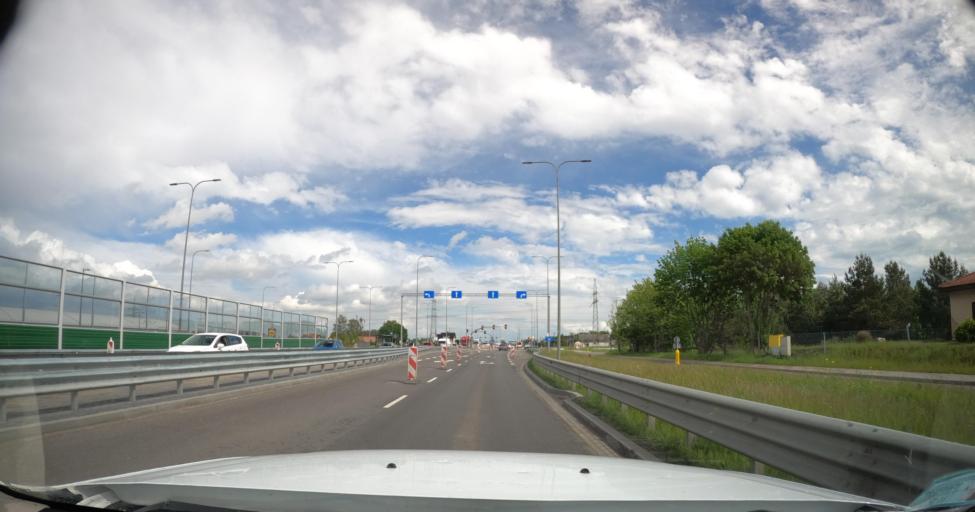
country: PL
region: Pomeranian Voivodeship
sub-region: Powiat gdanski
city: Lublewo Gdanskie
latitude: 54.3524
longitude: 18.4991
